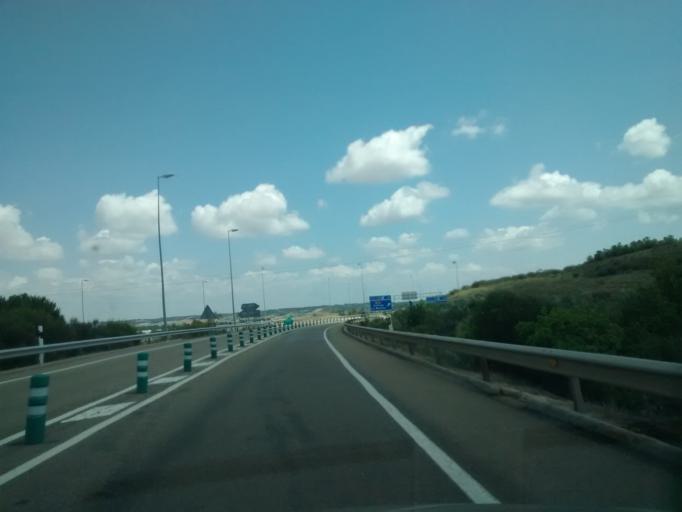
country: ES
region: Castille and Leon
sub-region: Provincia de Leon
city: Astorga
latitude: 42.4366
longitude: -6.0498
